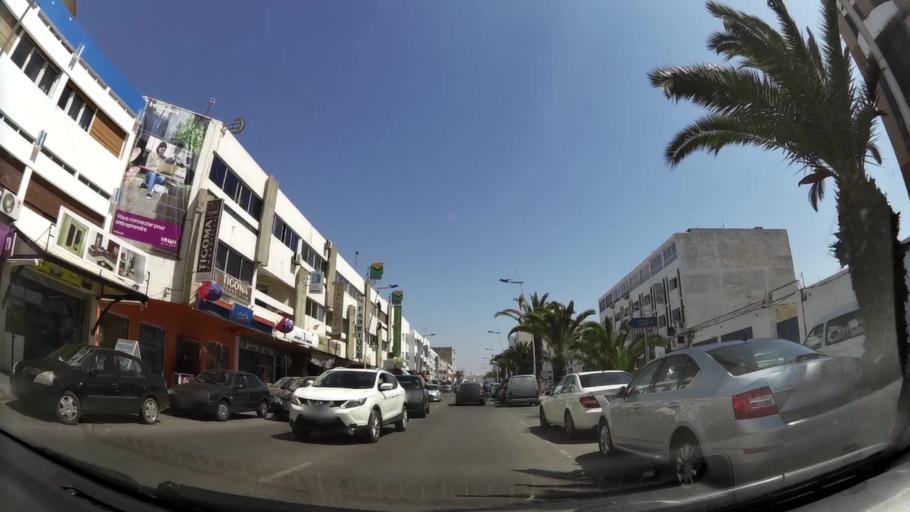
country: MA
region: Souss-Massa-Draa
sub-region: Agadir-Ida-ou-Tnan
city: Agadir
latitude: 30.4140
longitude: -9.5933
